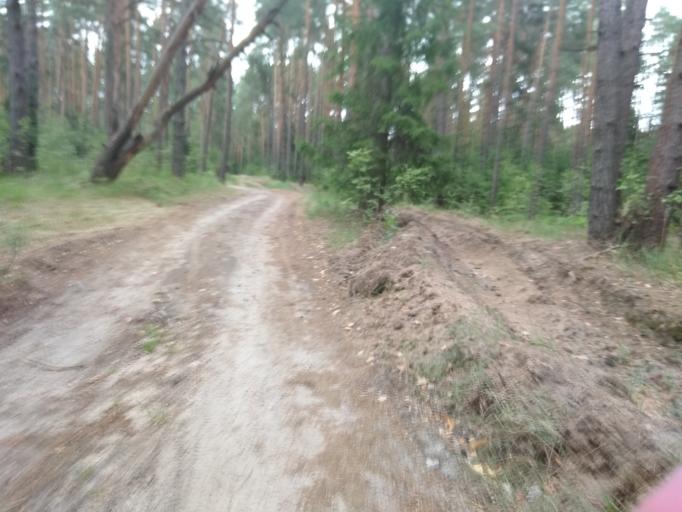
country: RU
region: Moskovskaya
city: Misheronskiy
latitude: 55.6262
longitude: 39.7183
